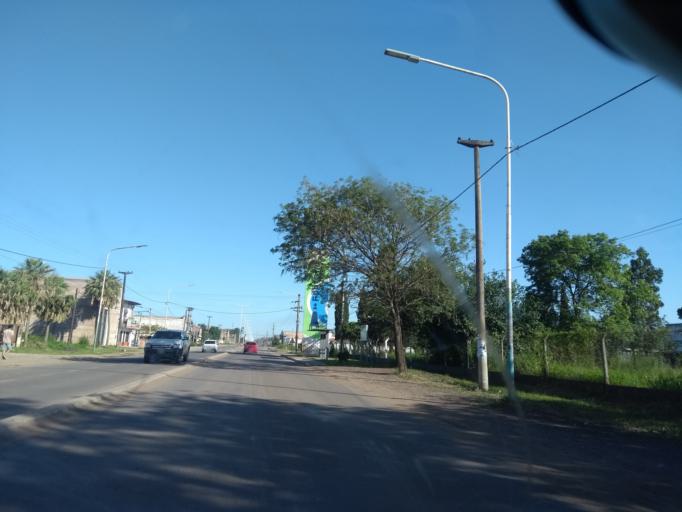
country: AR
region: Chaco
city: Fontana
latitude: -27.4306
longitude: -59.0241
